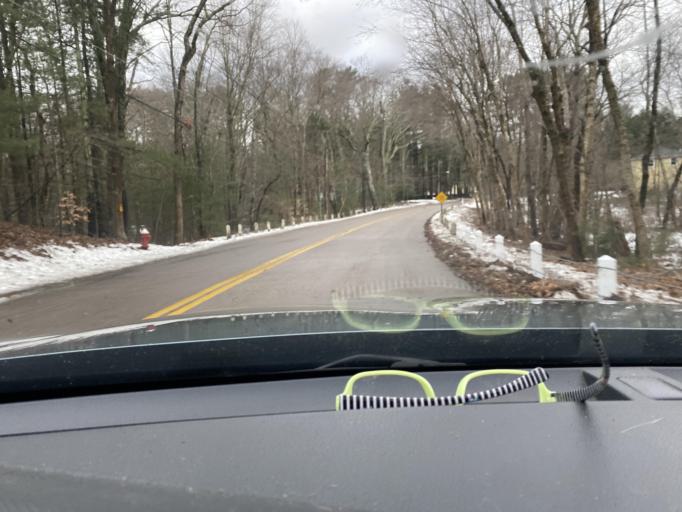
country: US
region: Massachusetts
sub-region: Middlesex County
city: Holliston
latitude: 42.2055
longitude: -71.3921
